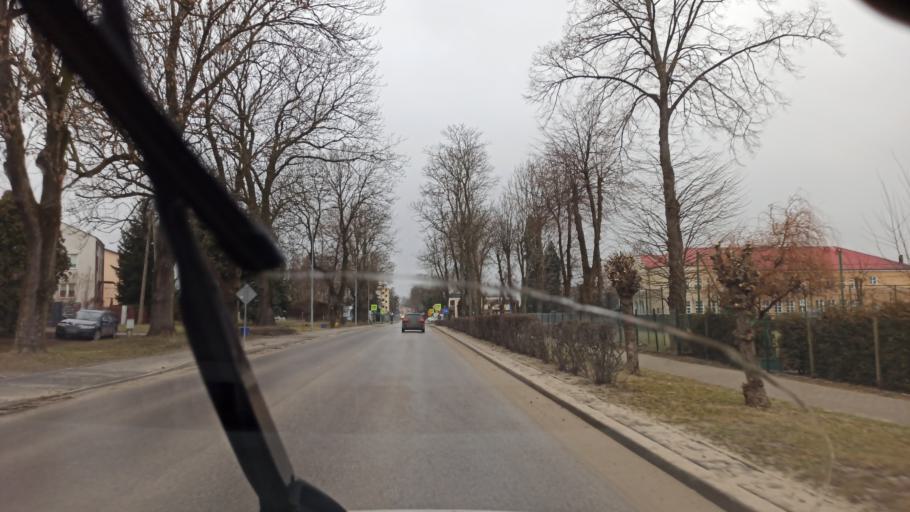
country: PL
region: Lublin Voivodeship
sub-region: Powiat lubelski
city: Bychawa
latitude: 51.0115
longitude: 22.5432
